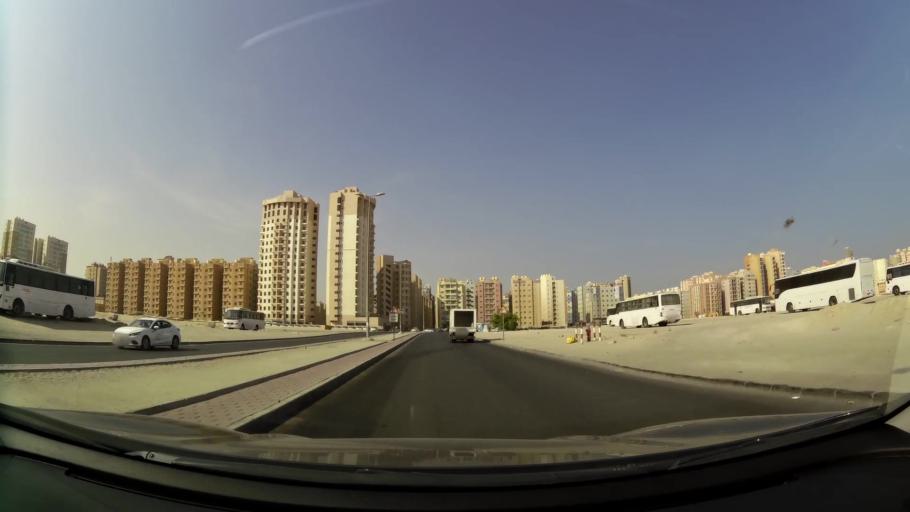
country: KW
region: Al Ahmadi
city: Al Mahbulah
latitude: 29.1419
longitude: 48.1207
